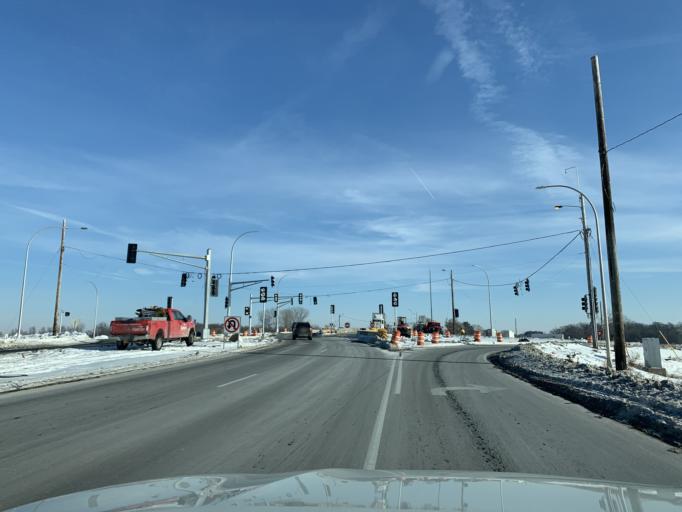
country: US
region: Minnesota
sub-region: Anoka County
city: Columbus
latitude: 45.2504
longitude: -93.0268
